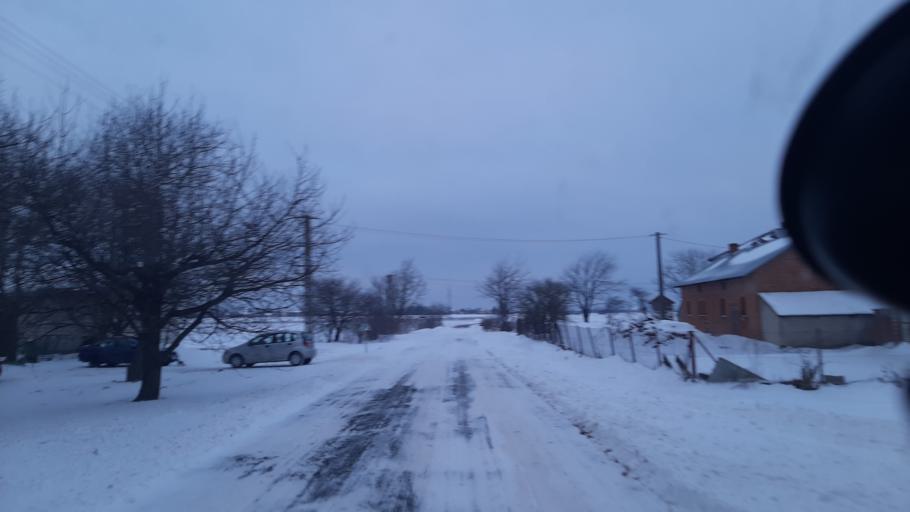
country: PL
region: Lublin Voivodeship
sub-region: Powiat lubelski
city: Jastkow
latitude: 51.3460
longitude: 22.4095
